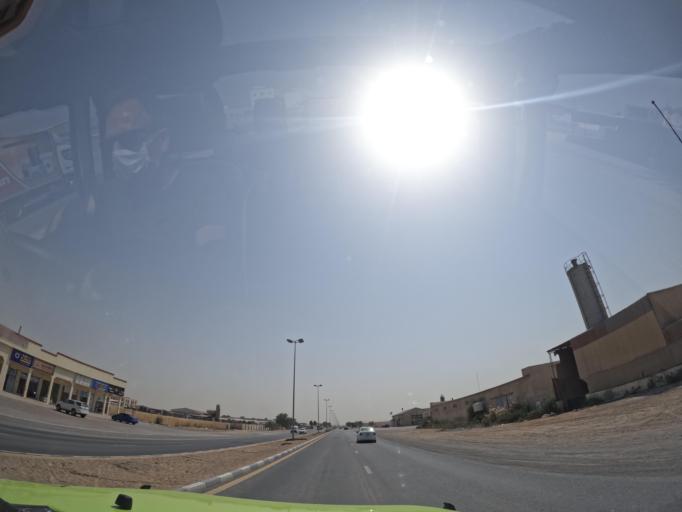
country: AE
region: Umm al Qaywayn
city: Umm al Qaywayn
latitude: 25.5085
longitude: 55.5591
